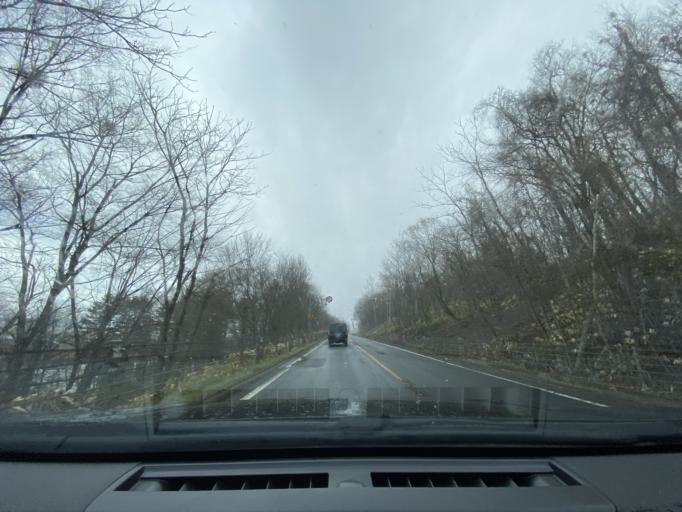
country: JP
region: Hokkaido
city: Fukagawa
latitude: 43.7057
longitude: 142.1020
